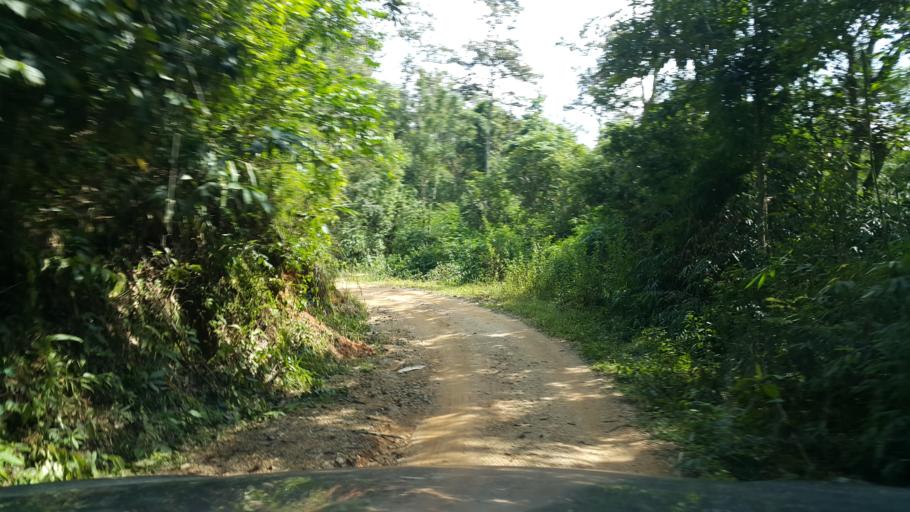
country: TH
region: Chiang Mai
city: Phrao
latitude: 19.1026
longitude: 99.2710
